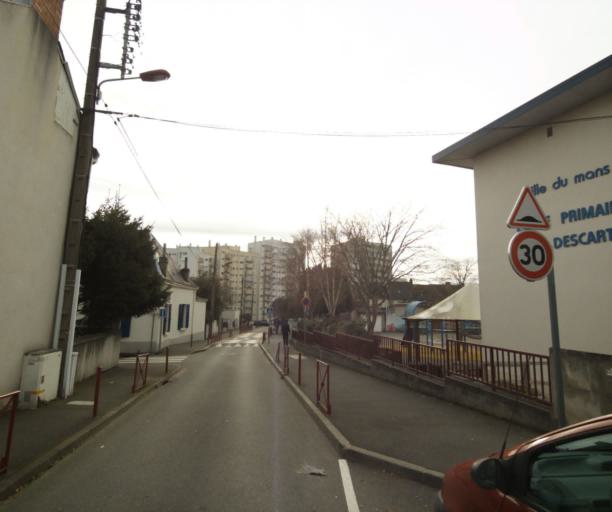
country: FR
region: Pays de la Loire
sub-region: Departement de la Sarthe
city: Le Mans
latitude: 47.9987
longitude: 0.2156
